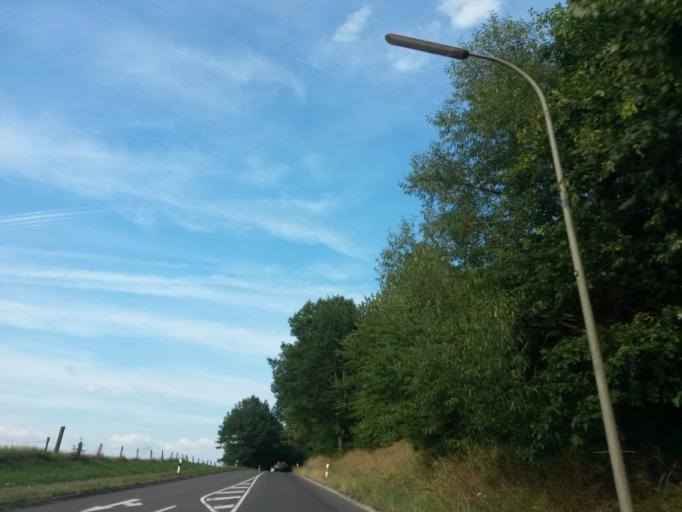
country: DE
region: North Rhine-Westphalia
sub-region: Regierungsbezirk Koln
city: Lindlar
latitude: 51.0311
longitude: 7.4031
